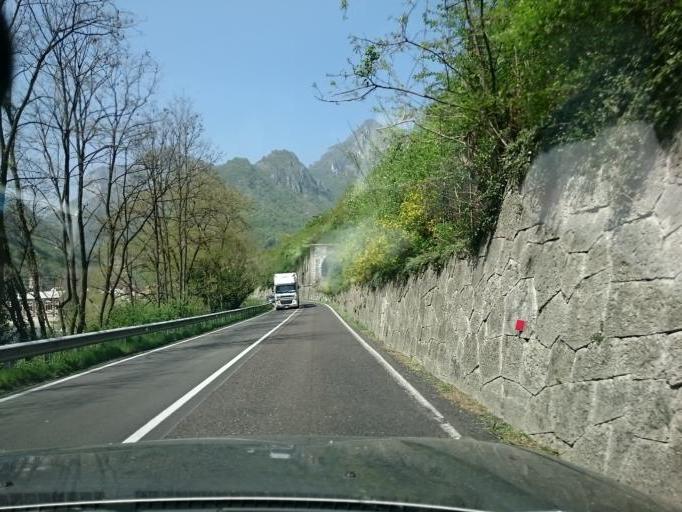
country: IT
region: Veneto
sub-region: Provincia di Vicenza
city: Valstagna
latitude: 45.8553
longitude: 11.6645
